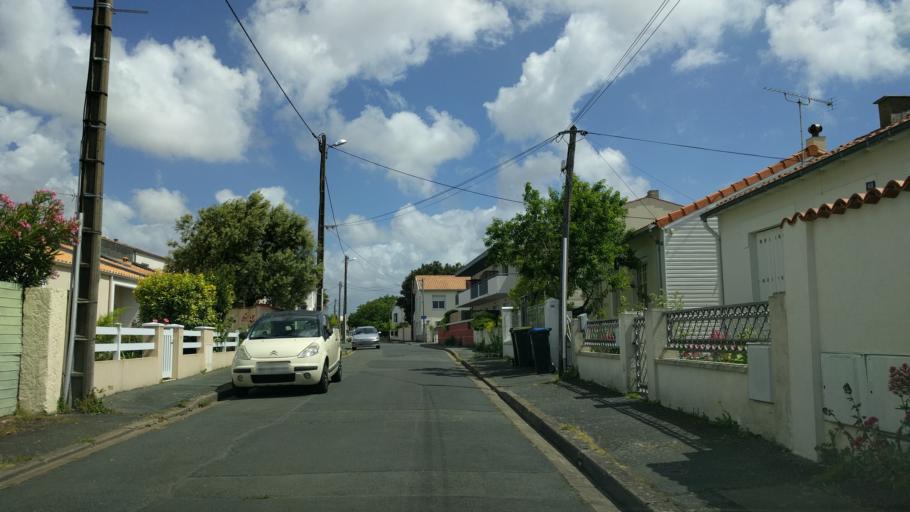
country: FR
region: Poitou-Charentes
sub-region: Departement de la Charente-Maritime
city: La Rochelle
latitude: 46.1720
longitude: -1.1418
